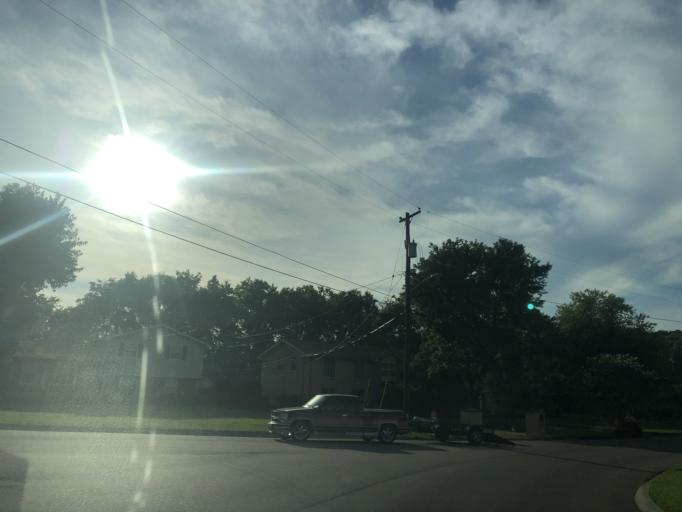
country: US
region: Tennessee
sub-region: Davidson County
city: Nashville
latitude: 36.2176
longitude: -86.8567
